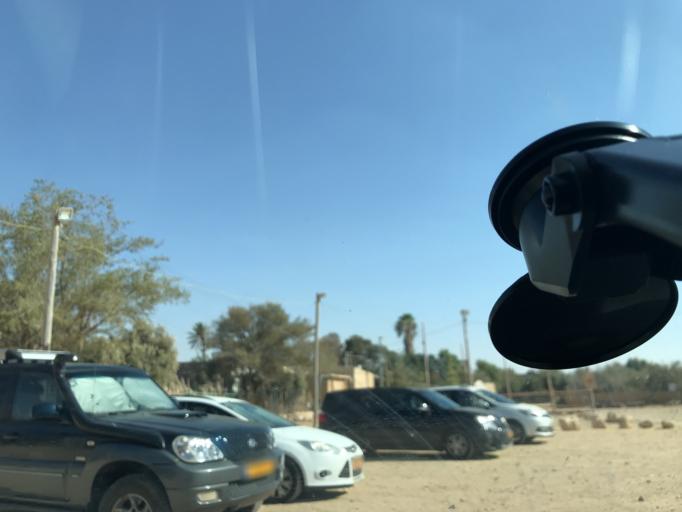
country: IL
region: Southern District
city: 'Arad
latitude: 31.3055
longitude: 35.2687
